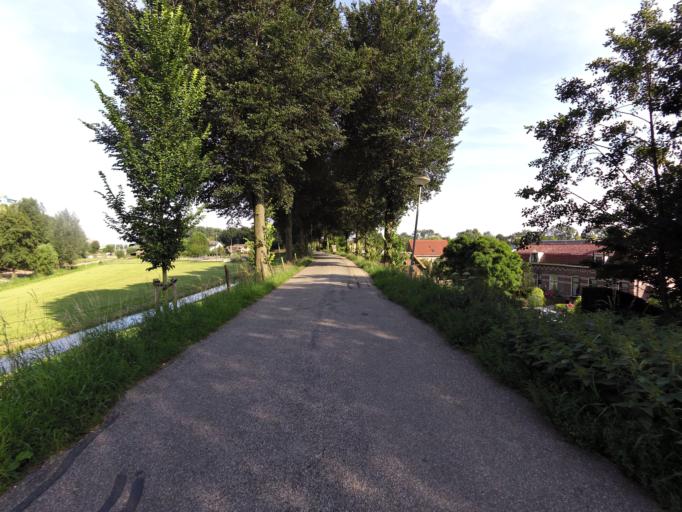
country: NL
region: South Holland
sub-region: Gemeente Dordrecht
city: Dordrecht
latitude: 51.8024
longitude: 4.7081
